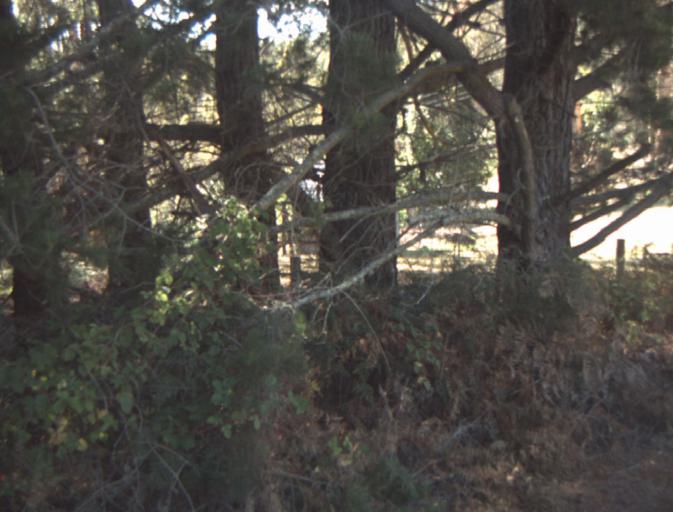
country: AU
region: Tasmania
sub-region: Launceston
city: Mayfield
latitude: -41.2951
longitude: 147.1987
